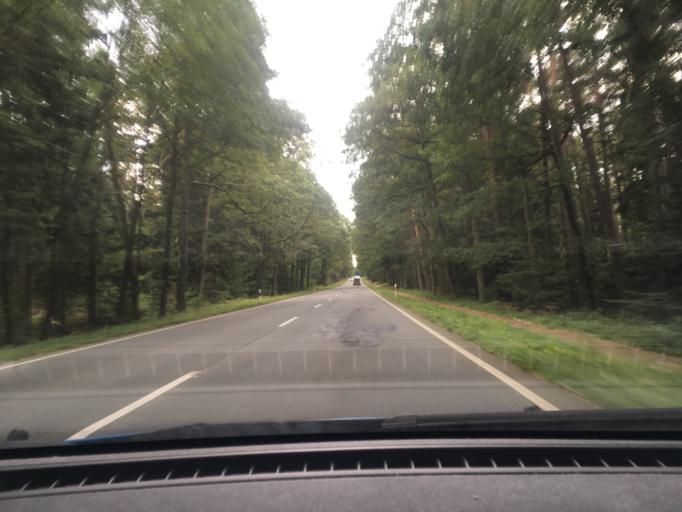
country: DE
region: Lower Saxony
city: Suderburg
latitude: 52.8440
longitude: 10.4887
